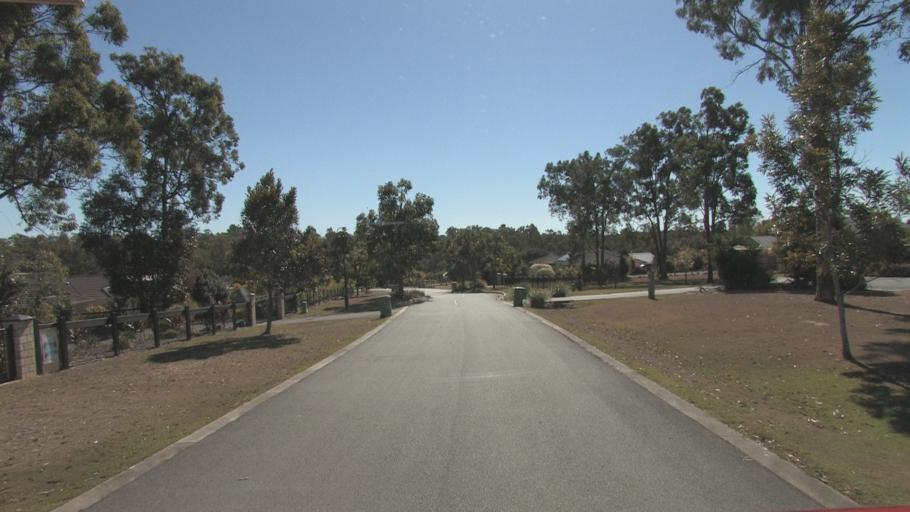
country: AU
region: Queensland
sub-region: Logan
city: North Maclean
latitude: -27.7586
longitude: 152.9624
